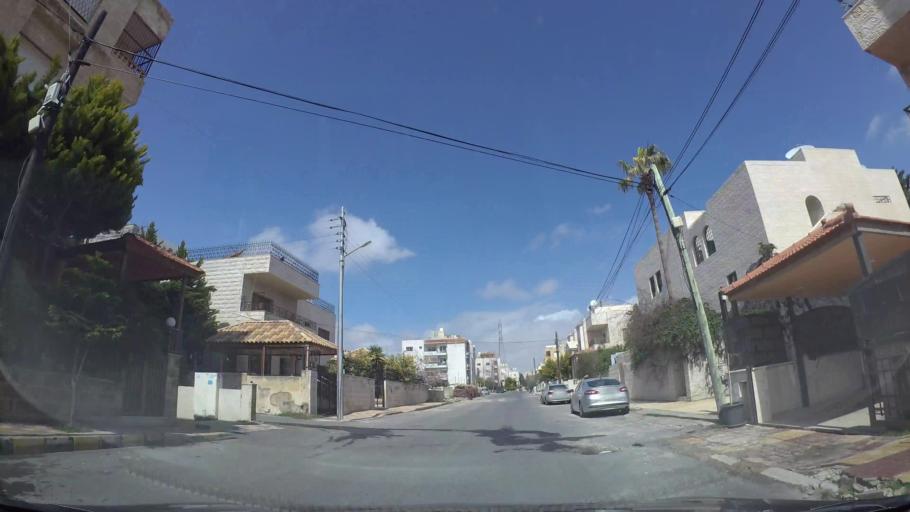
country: JO
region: Amman
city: Wadi as Sir
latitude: 31.9600
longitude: 35.8426
